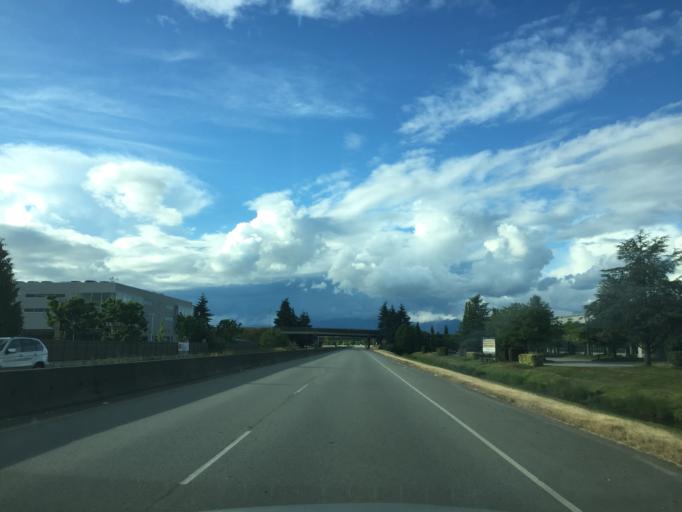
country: CA
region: British Columbia
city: Richmond
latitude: 49.1732
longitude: -123.0744
